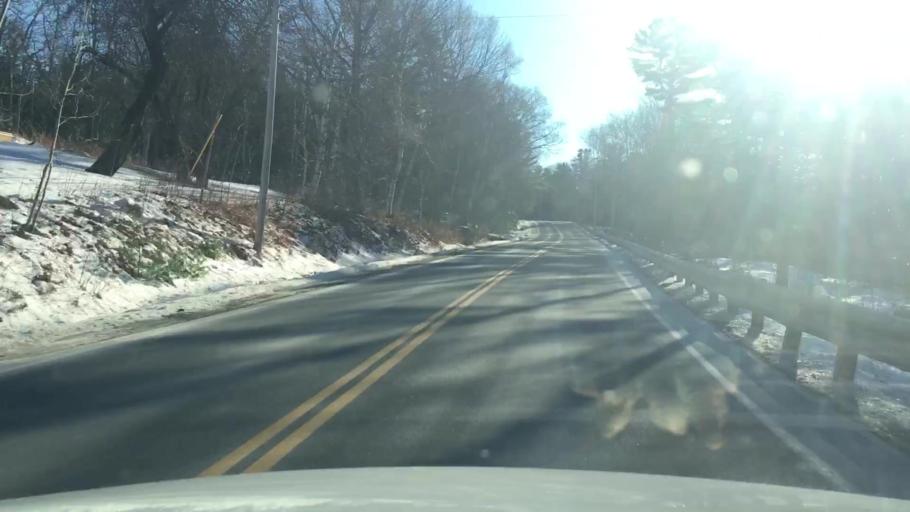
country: US
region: Maine
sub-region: Hancock County
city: Orland
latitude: 44.5407
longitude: -68.7455
